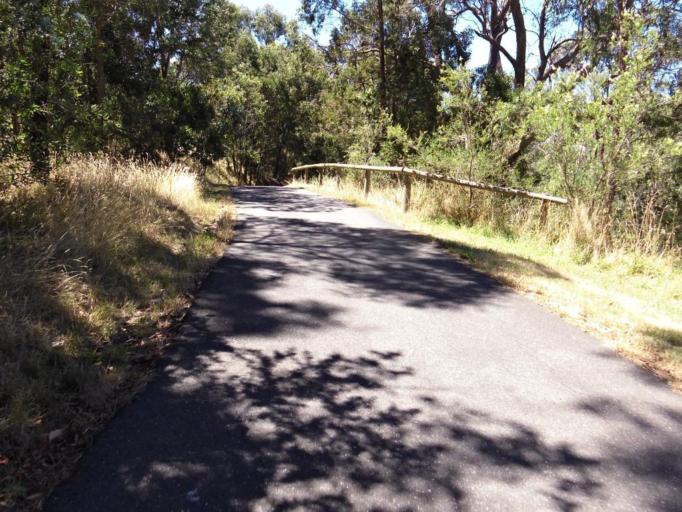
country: AU
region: Victoria
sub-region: Hume
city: Sunbury
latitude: -37.3573
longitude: 144.5378
